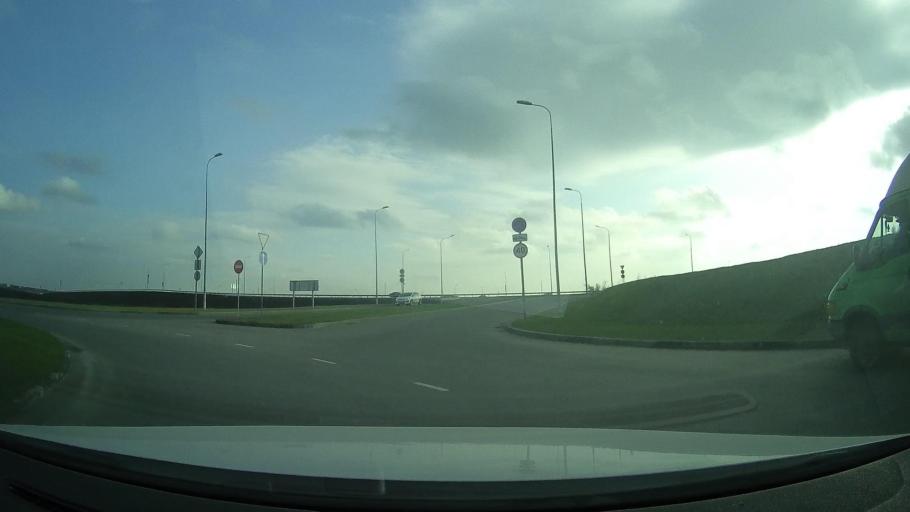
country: RU
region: Rostov
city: Grushevskaya
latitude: 47.4868
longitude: 39.9334
